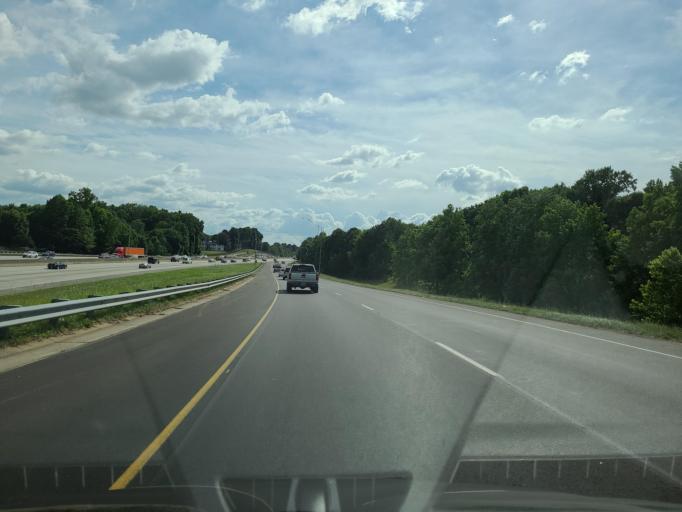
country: US
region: North Carolina
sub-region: Mecklenburg County
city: Charlotte
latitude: 35.2840
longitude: -80.7772
